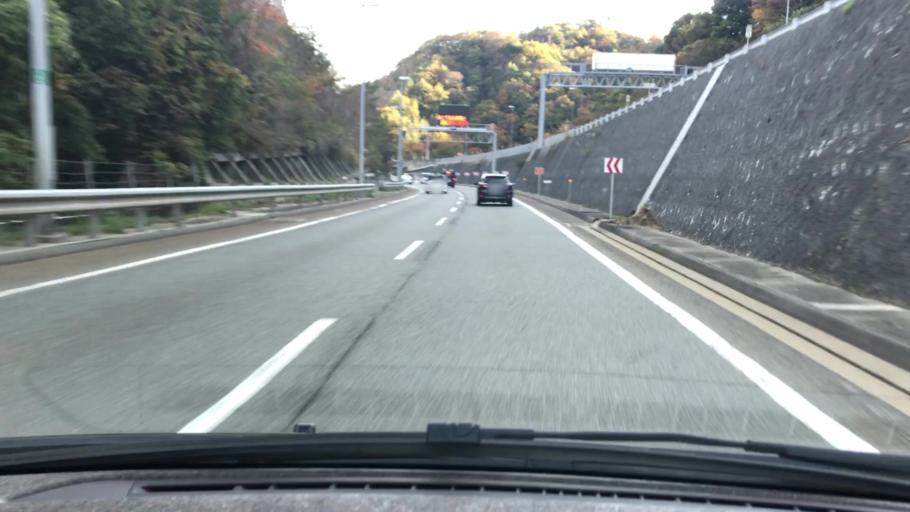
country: JP
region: Hyogo
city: Sandacho
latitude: 34.7898
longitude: 135.2220
